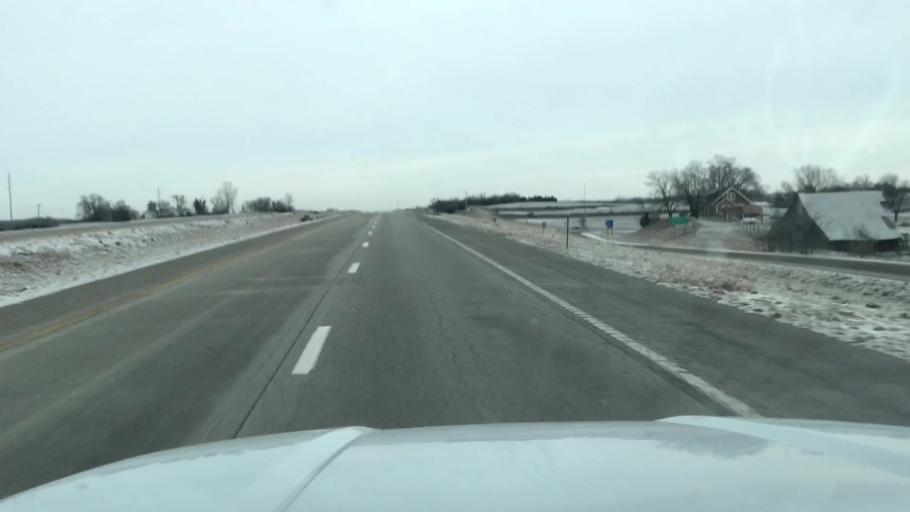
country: US
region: Missouri
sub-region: Andrew County
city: Savannah
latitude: 39.9205
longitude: -94.8601
